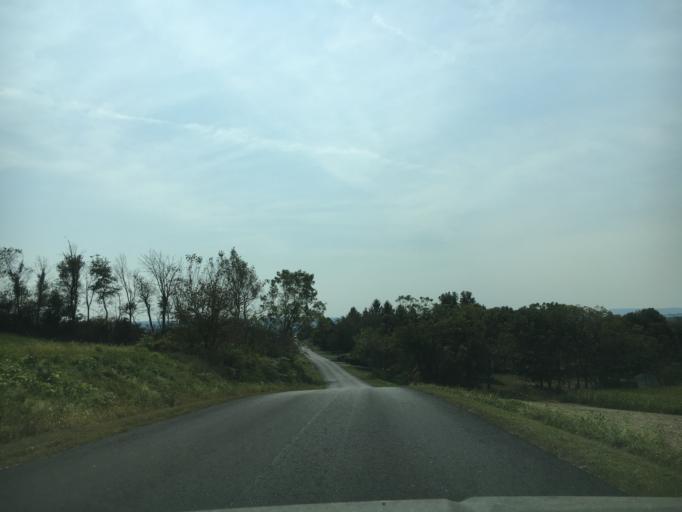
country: US
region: Pennsylvania
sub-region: Berks County
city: Topton
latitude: 40.5439
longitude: -75.7161
